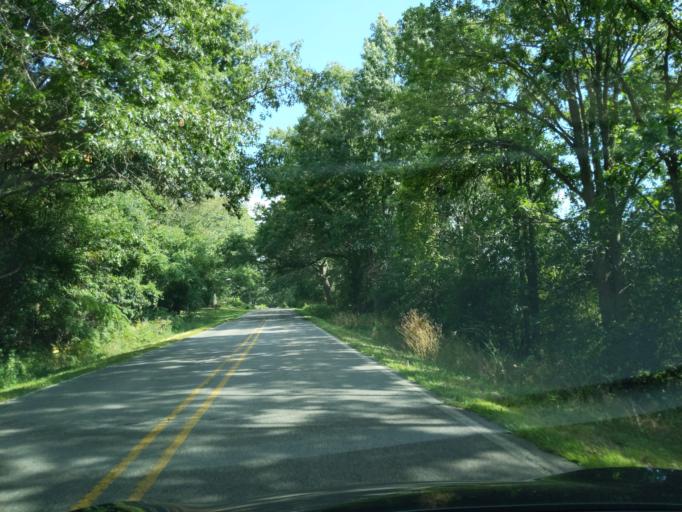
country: US
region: Michigan
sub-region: Jackson County
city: Jackson
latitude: 42.2936
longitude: -84.4823
